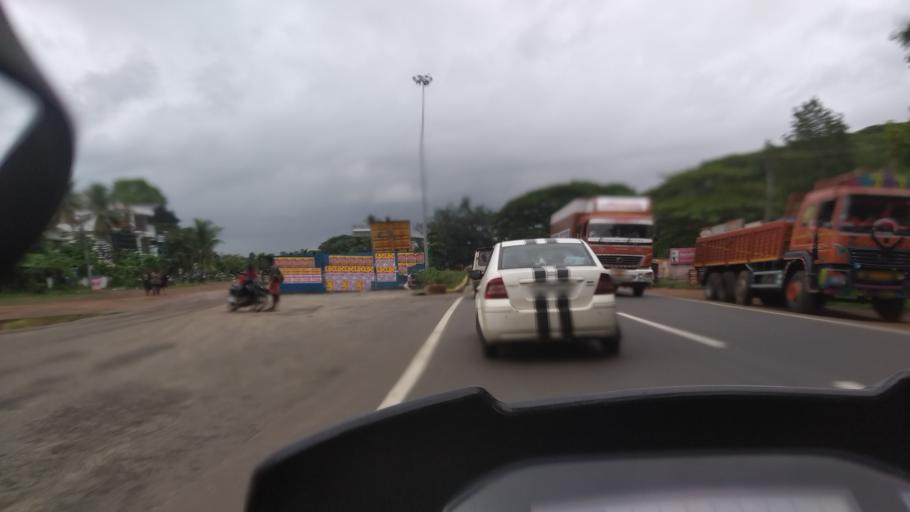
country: IN
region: Kerala
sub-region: Alappuzha
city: Alleppey
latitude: 9.4669
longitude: 76.3389
